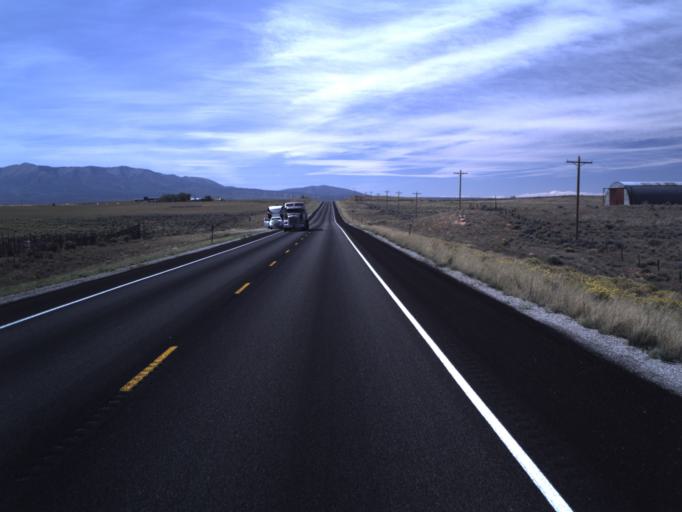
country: US
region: Utah
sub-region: San Juan County
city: Monticello
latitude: 37.8494
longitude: -109.1615
